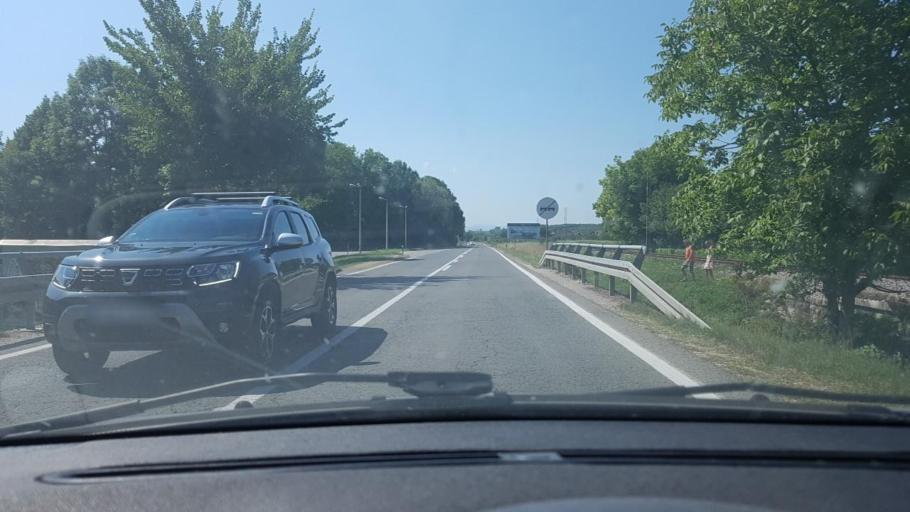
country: BA
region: Federation of Bosnia and Herzegovina
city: Bihac
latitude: 44.8012
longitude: 15.9082
